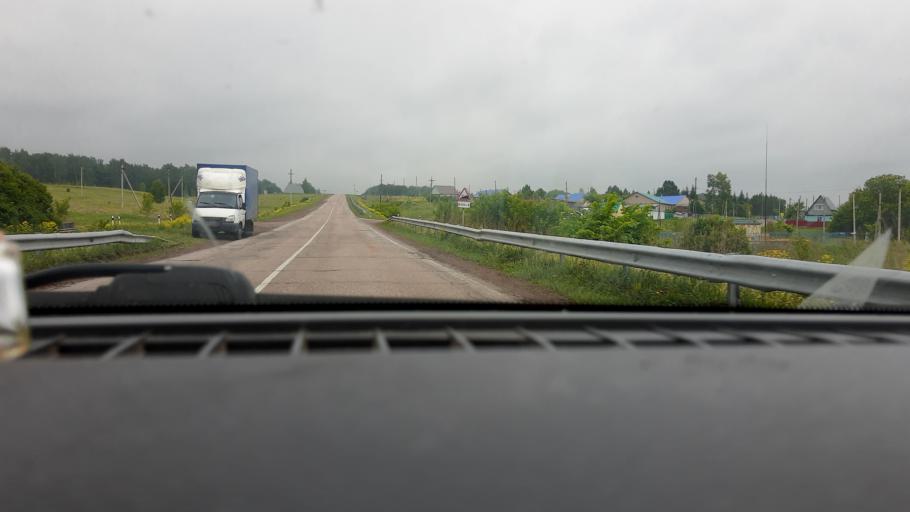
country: RU
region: Bashkortostan
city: Belebey
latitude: 54.1874
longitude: 54.0808
